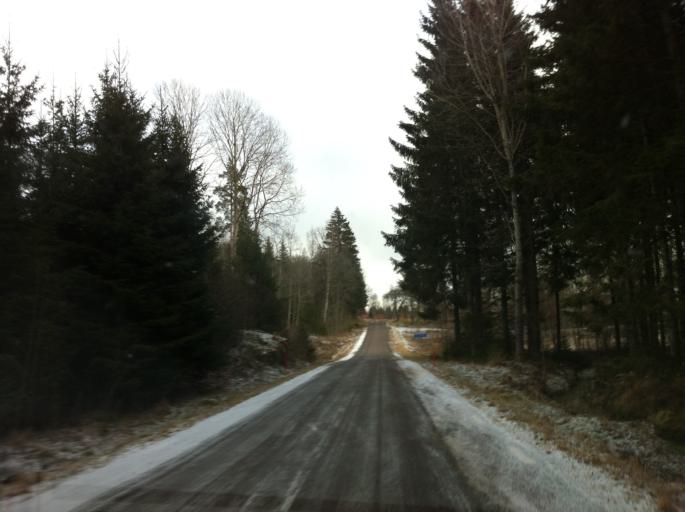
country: SE
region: Joenkoeping
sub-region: Eksjo Kommun
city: Mariannelund
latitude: 57.6109
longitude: 15.6926
